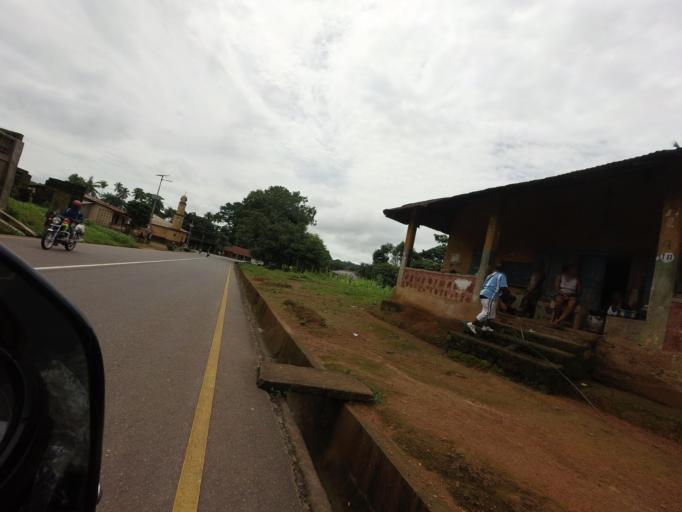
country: SL
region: Northern Province
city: Kambia
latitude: 9.1284
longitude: -12.9195
